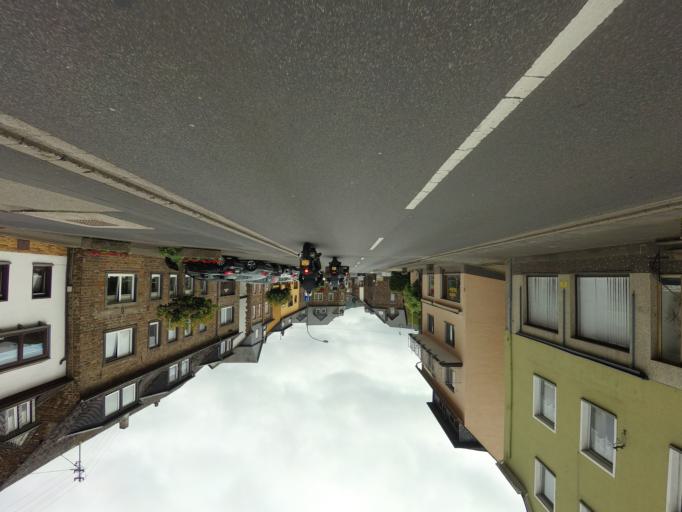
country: DE
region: Rheinland-Pfalz
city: Treis-Karden
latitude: 50.1753
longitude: 7.3017
